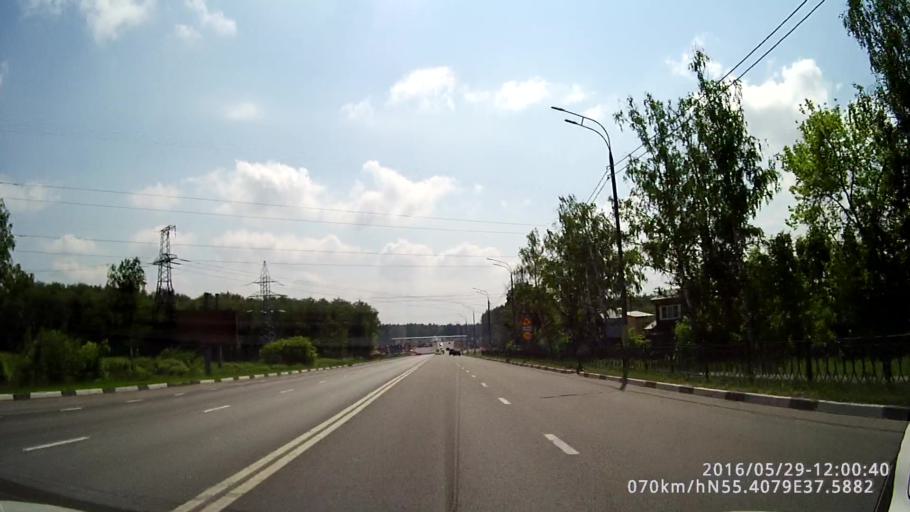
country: RU
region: Moskovskaya
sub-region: Podol'skiy Rayon
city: Podol'sk
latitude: 55.4076
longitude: 37.5886
